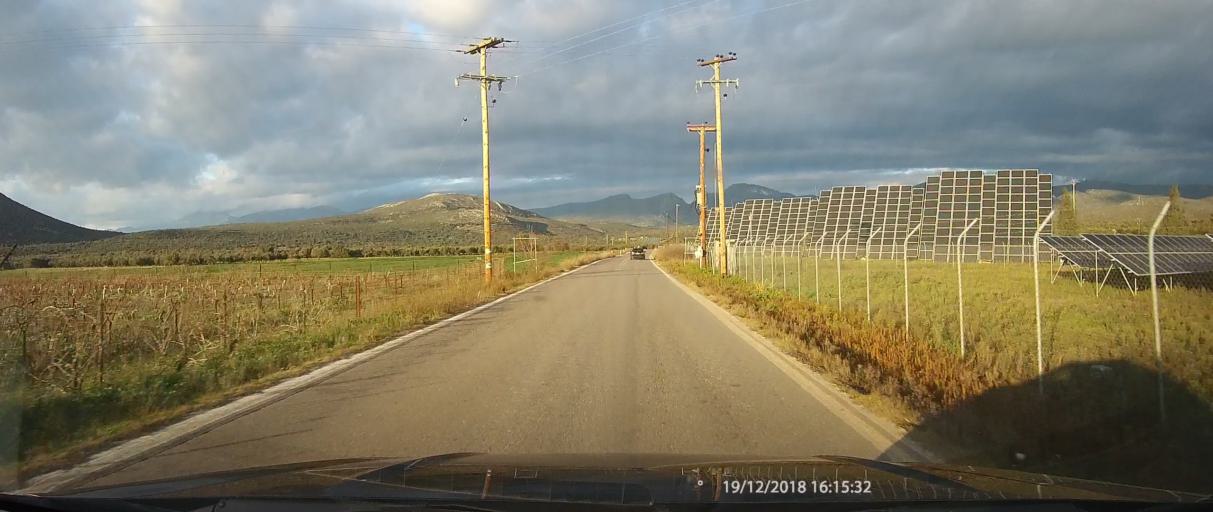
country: GR
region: Peloponnese
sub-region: Nomos Lakonias
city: Kato Glikovrisi
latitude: 36.8910
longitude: 22.8014
